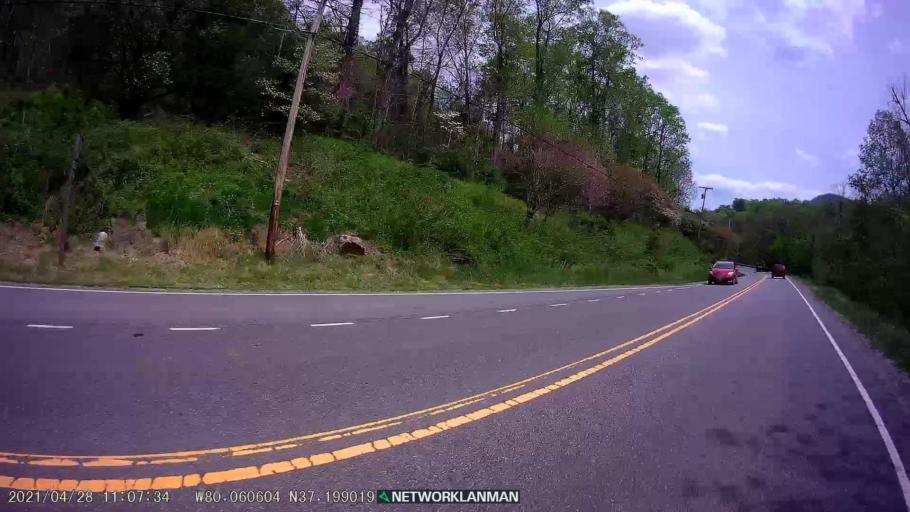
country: US
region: Virginia
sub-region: Roanoke County
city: Cave Spring
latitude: 37.1988
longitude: -80.0602
